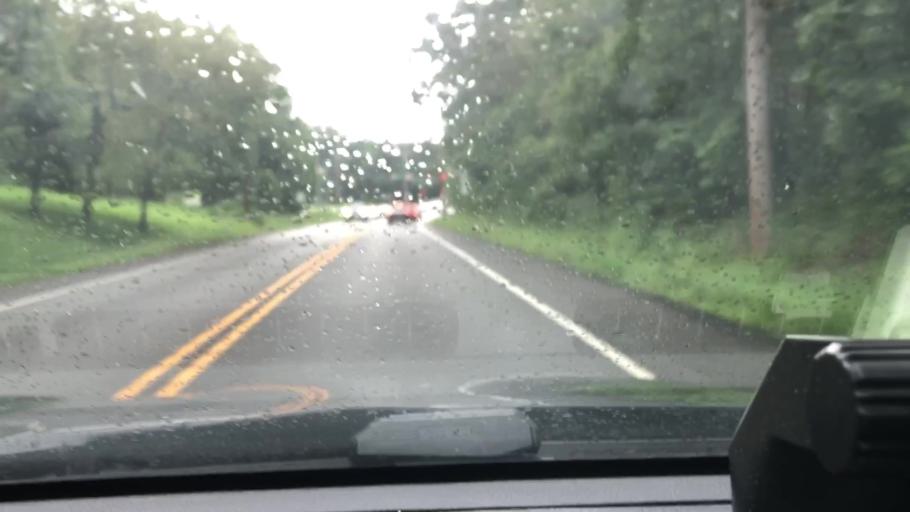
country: US
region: Pennsylvania
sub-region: Montgomery County
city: Pennsburg
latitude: 40.3898
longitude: -75.5051
